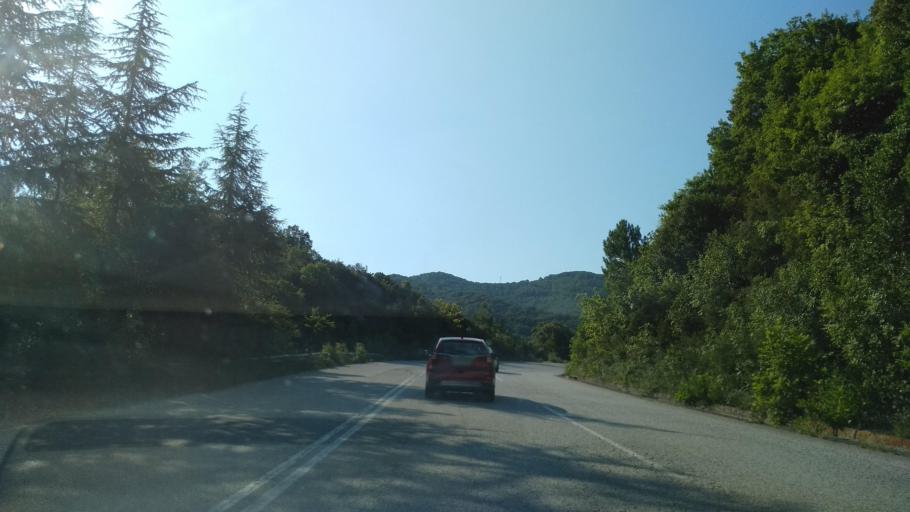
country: GR
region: Central Macedonia
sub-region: Nomos Chalkidikis
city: Stratonion
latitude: 40.5455
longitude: 23.8281
